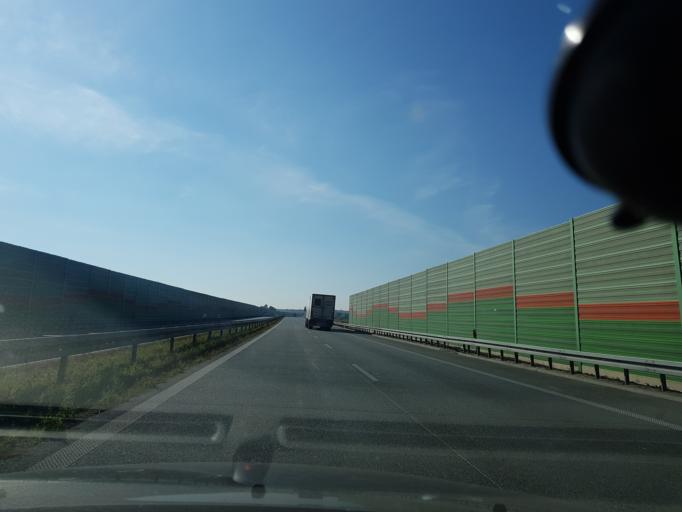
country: PL
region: Lodz Voivodeship
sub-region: Powiat tomaszowski
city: Lubochnia
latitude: 51.6033
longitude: 20.0595
